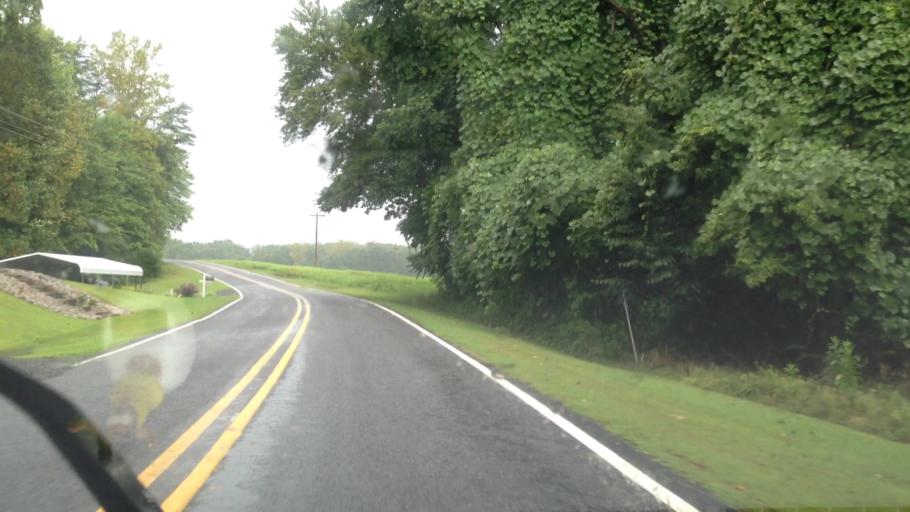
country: US
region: North Carolina
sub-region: Rockingham County
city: Mayodan
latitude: 36.4353
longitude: -80.0859
